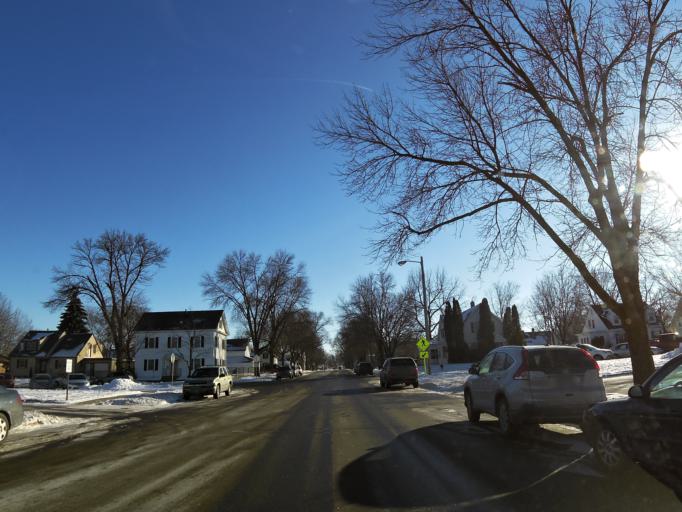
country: US
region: Minnesota
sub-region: Scott County
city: Shakopee
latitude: 44.7946
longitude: -93.5288
